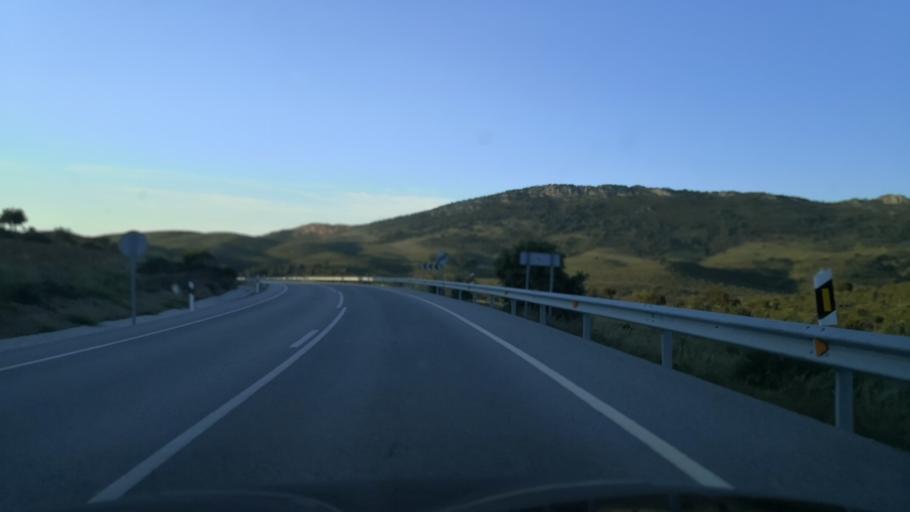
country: ES
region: Extremadura
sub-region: Provincia de Caceres
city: Valencia de Alcantara
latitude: 39.4614
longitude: -7.2033
